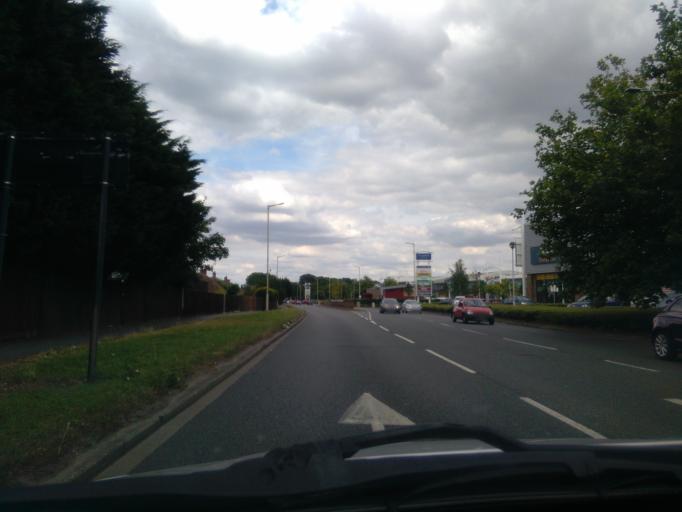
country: GB
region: England
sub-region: Bedford
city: Bedford
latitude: 52.1307
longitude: -0.4623
